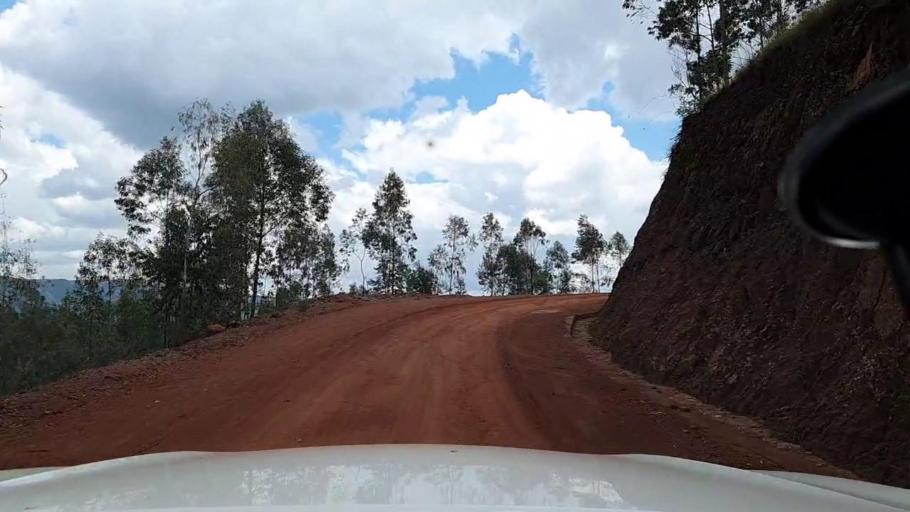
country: RW
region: Northern Province
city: Byumba
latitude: -1.7553
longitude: 29.8470
